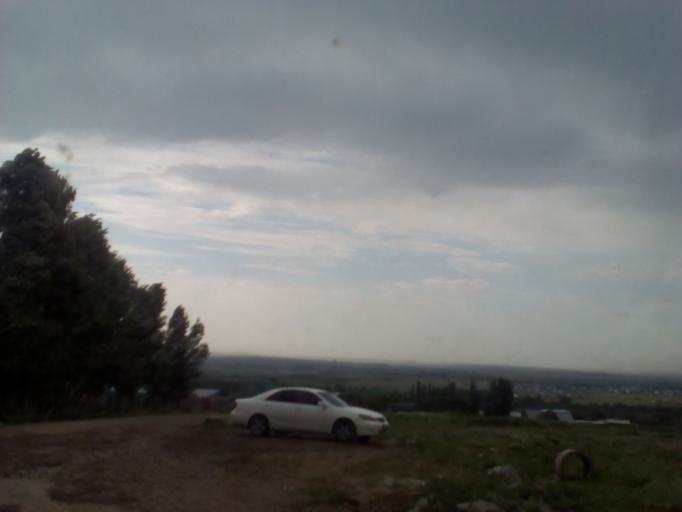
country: KZ
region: Almaty Oblysy
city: Burunday
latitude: 43.1501
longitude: 76.3858
